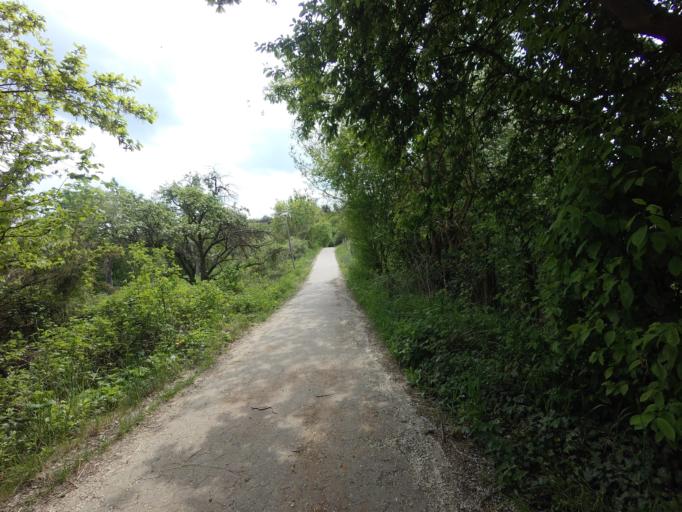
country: DE
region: Lower Saxony
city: Diekholzen
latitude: 52.1252
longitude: 9.9100
